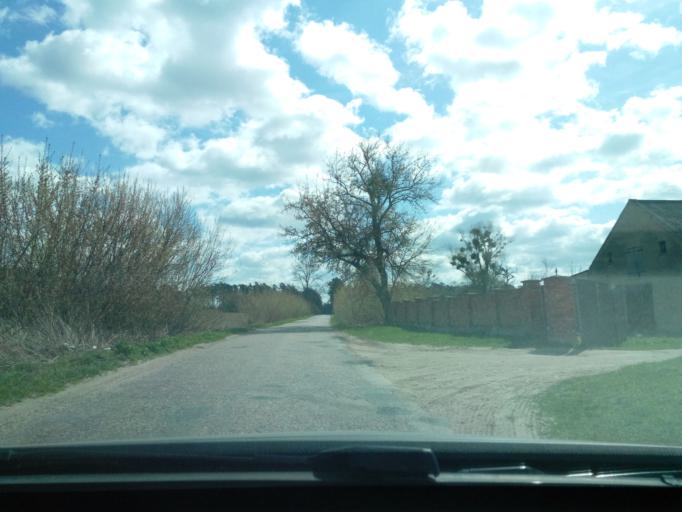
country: PL
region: Warmian-Masurian Voivodeship
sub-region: Powiat nowomiejski
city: Biskupiec
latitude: 53.4584
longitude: 19.2801
